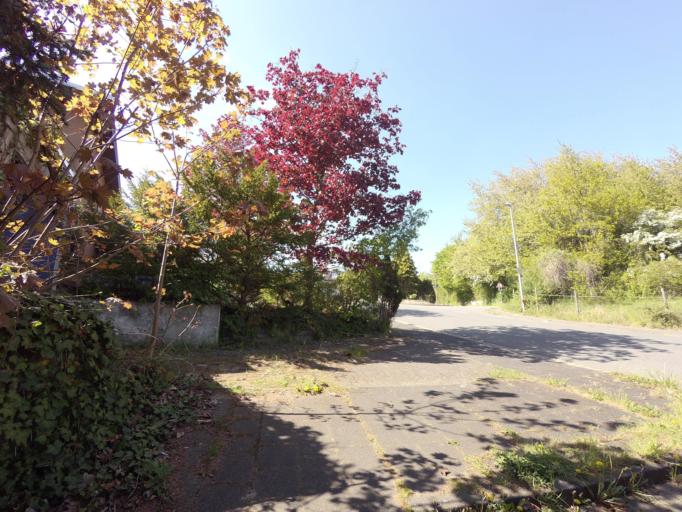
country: DE
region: Lower Saxony
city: Diekholzen
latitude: 52.1290
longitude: 9.9098
